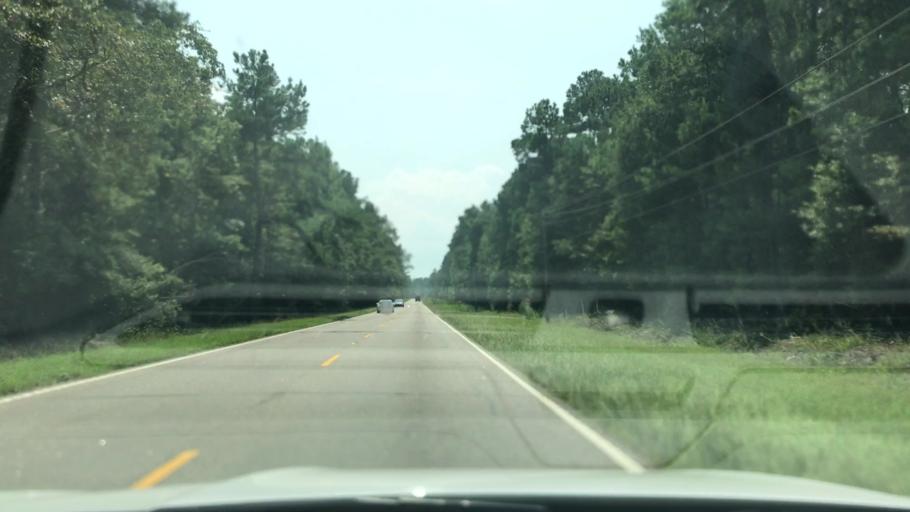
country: US
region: South Carolina
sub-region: Georgetown County
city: Georgetown
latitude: 33.4929
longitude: -79.2635
